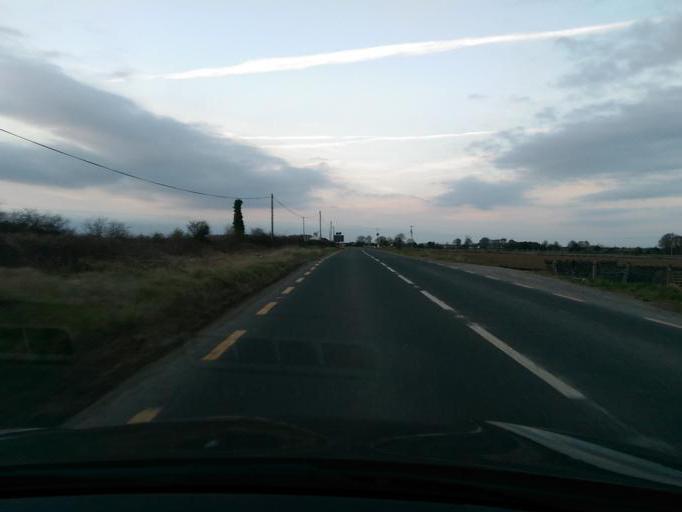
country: IE
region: Connaught
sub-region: County Galway
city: Portumna
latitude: 53.0164
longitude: -8.1253
